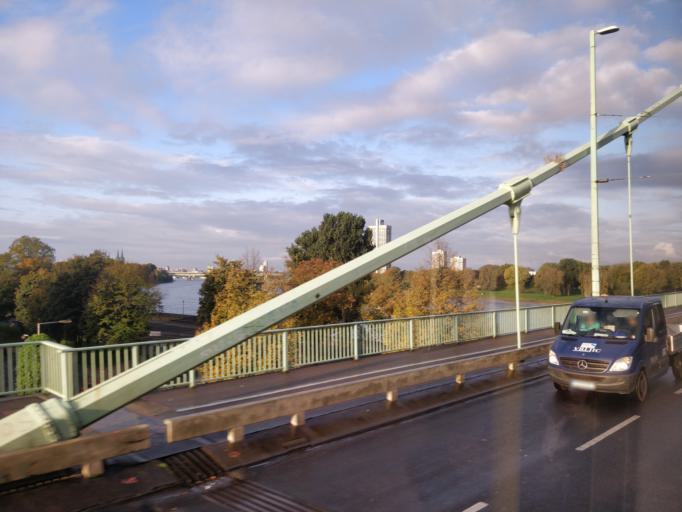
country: DE
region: North Rhine-Westphalia
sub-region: Regierungsbezirk Koln
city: Muelheim
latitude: 50.9633
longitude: 6.9986
